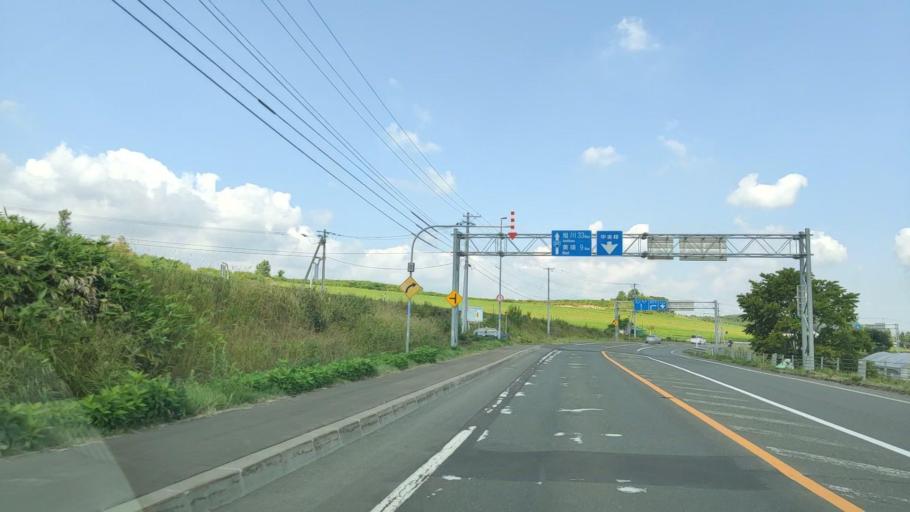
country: JP
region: Hokkaido
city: Shimo-furano
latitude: 43.5323
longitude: 142.4417
